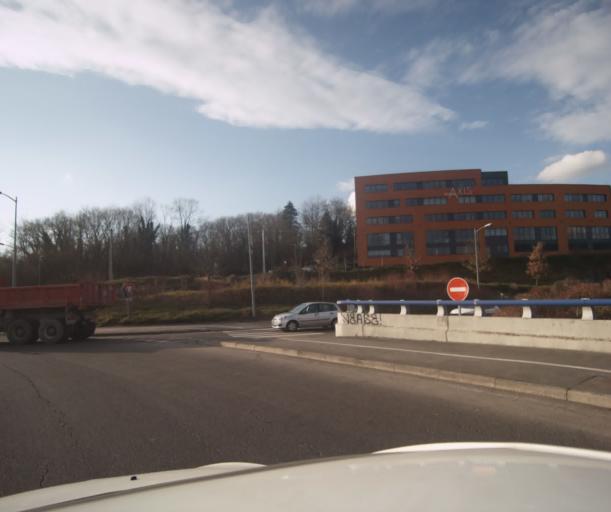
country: FR
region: Franche-Comte
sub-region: Departement du Doubs
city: Besancon
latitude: 47.2624
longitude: 6.0054
